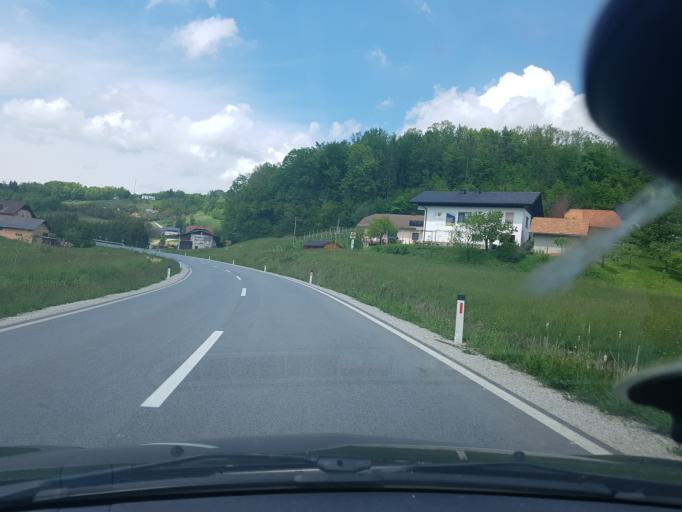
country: SI
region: Rogaska Slatina
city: Rogaska Slatina
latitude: 46.2401
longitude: 15.6702
